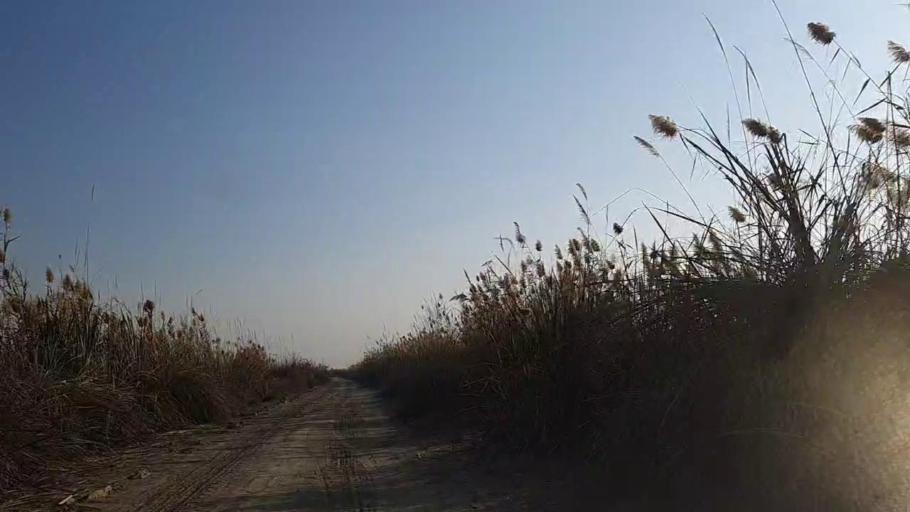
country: PK
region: Sindh
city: Daur
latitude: 26.4347
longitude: 68.3525
